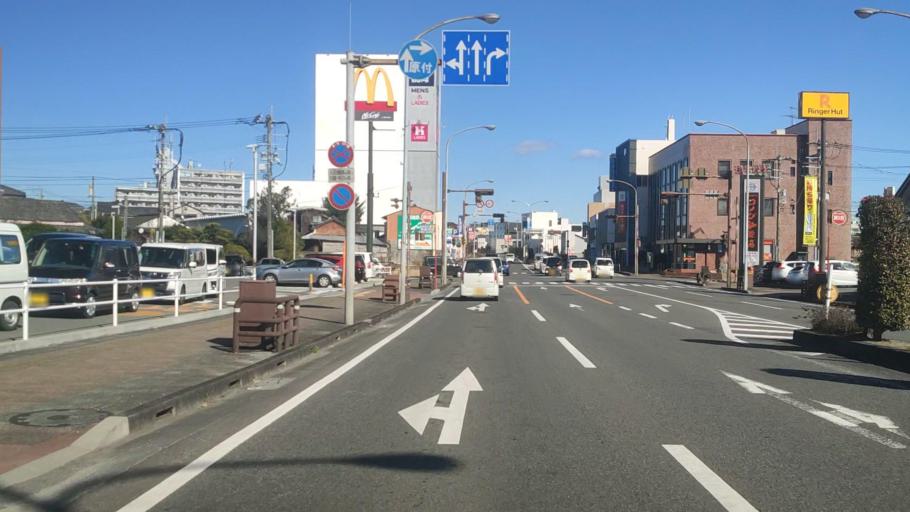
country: JP
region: Miyazaki
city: Miyakonojo
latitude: 31.7286
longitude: 131.0662
